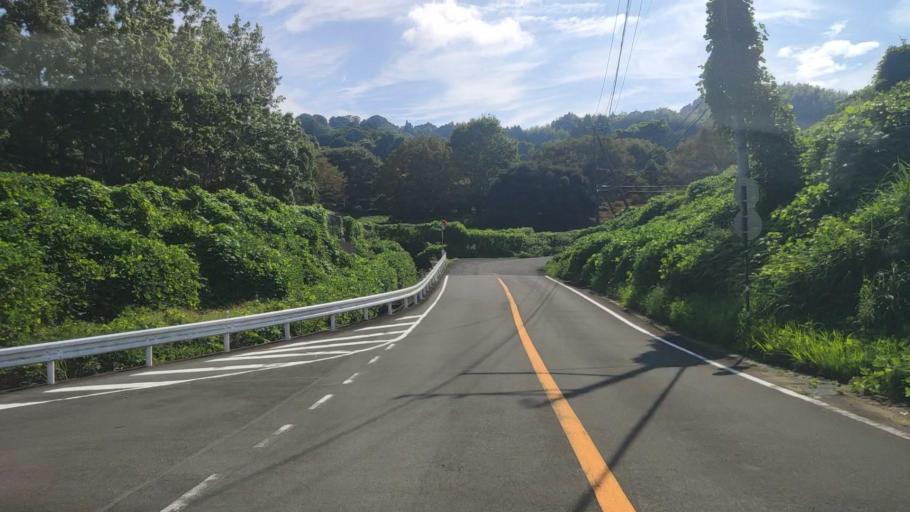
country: JP
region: Shizuoka
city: Shizuoka-shi
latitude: 34.9856
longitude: 138.4767
